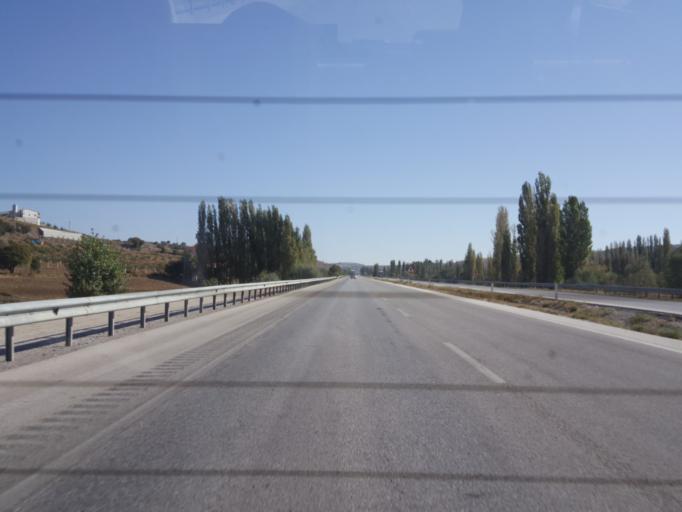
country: TR
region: Corum
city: Bogazkale
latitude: 40.2511
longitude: 34.6054
